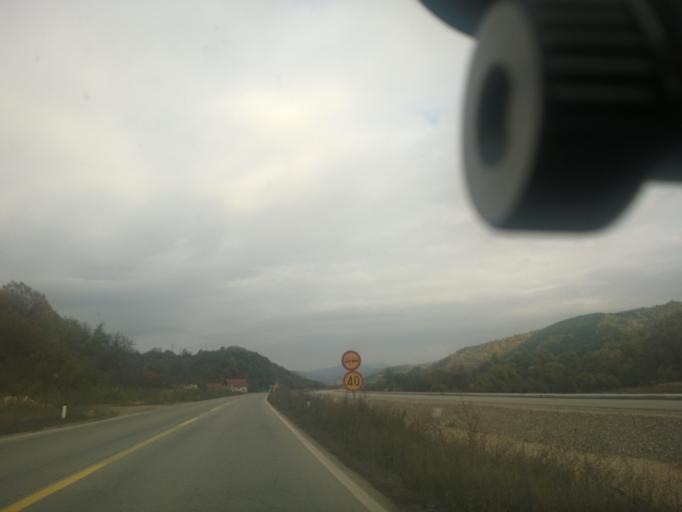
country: RS
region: Central Serbia
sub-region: Pirotski Okrug
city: Pirot
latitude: 43.1796
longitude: 22.5679
